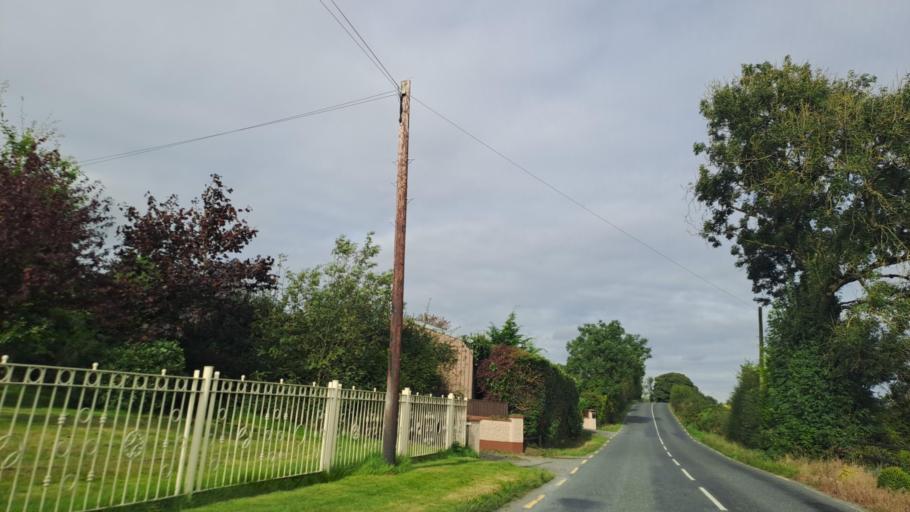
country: IE
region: Ulster
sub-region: An Cabhan
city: Kingscourt
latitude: 53.9818
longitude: -6.8810
